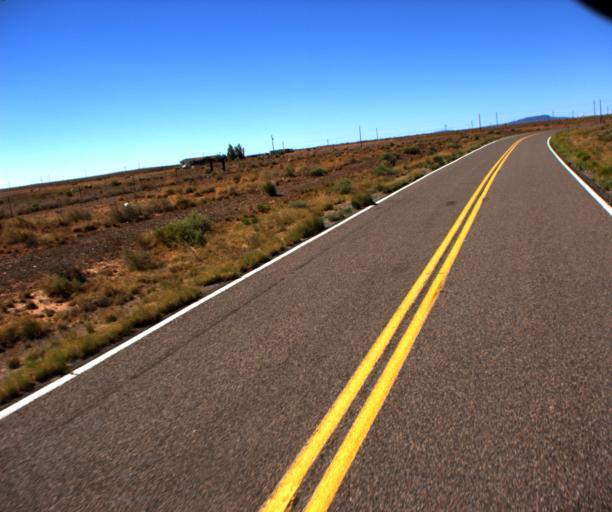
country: US
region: Arizona
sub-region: Coconino County
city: LeChee
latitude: 35.0891
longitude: -110.8607
